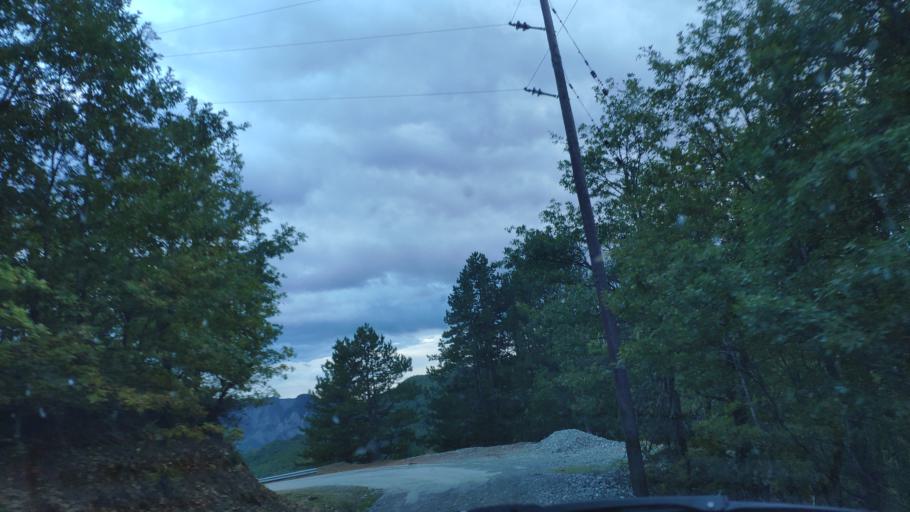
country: AL
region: Korce
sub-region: Rrethi i Kolonjes
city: Erseke
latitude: 40.2592
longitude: 20.8577
